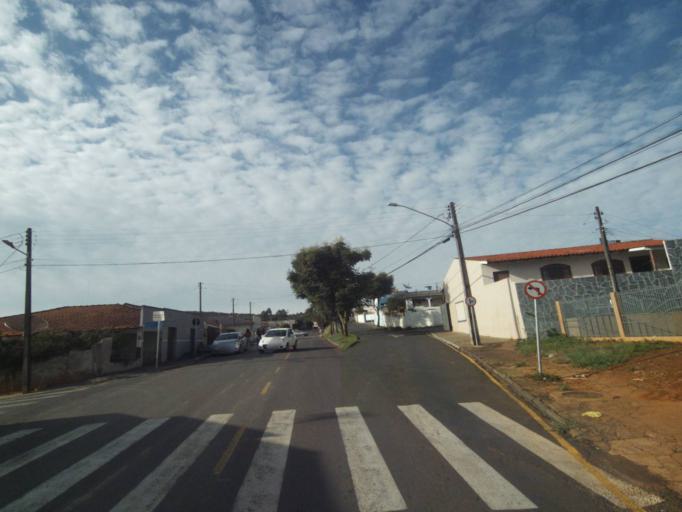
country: BR
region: Parana
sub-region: Telemaco Borba
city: Telemaco Borba
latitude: -24.3461
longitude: -50.6124
